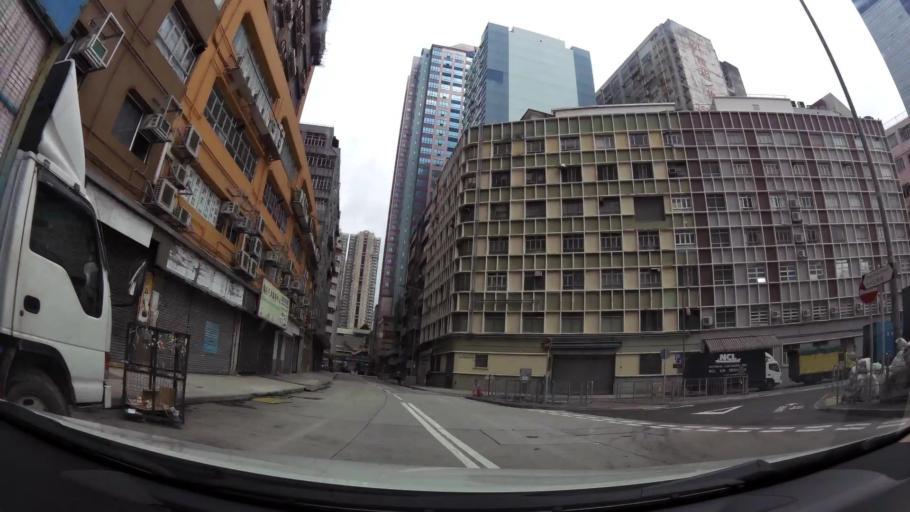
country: HK
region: Wong Tai Sin
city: Wong Tai Sin
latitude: 22.3357
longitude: 114.1982
